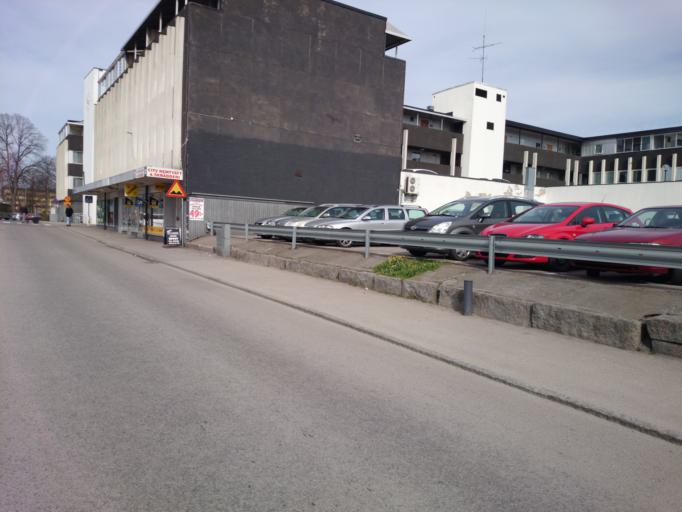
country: SE
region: Kronoberg
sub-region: Vaxjo Kommun
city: Vaexjoe
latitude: 56.8773
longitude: 14.8059
